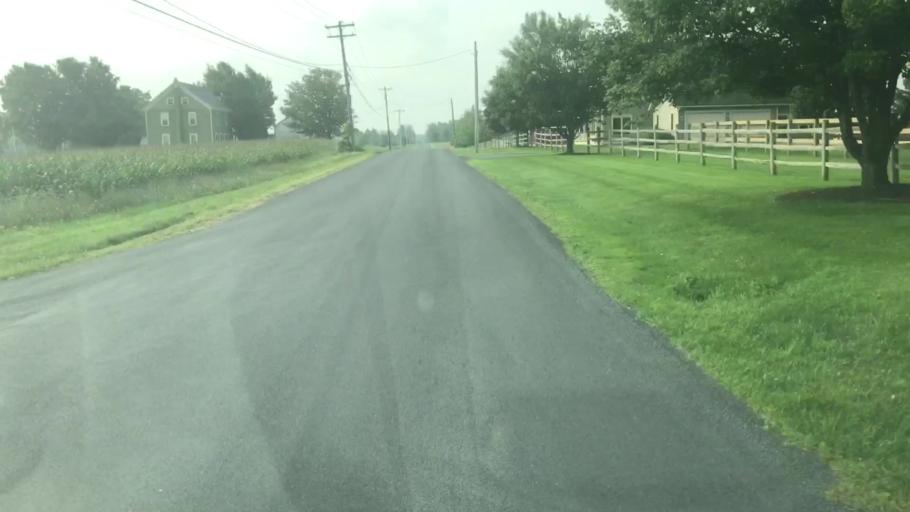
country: US
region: New York
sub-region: Onondaga County
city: Skaneateles
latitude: 42.9284
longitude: -76.4573
